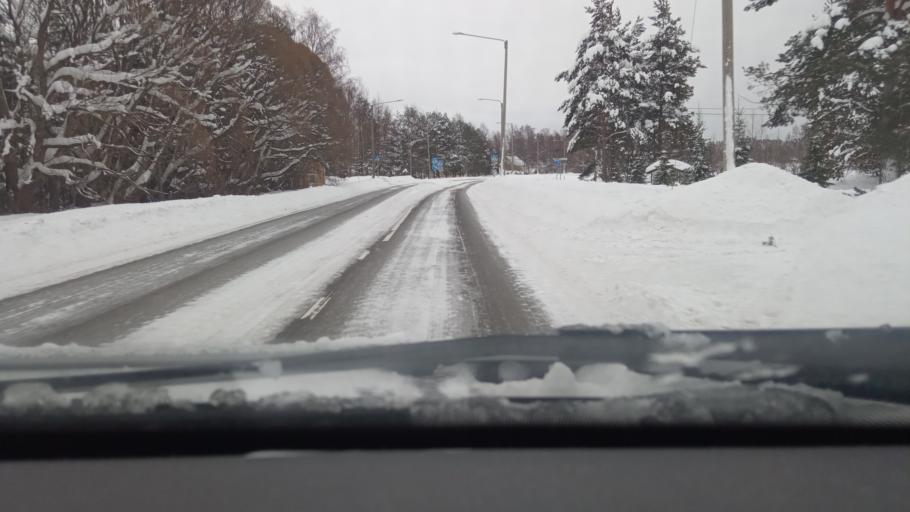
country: FI
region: Southern Ostrobothnia
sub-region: Jaerviseutu
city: Alajaervi
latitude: 62.9932
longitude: 23.8308
